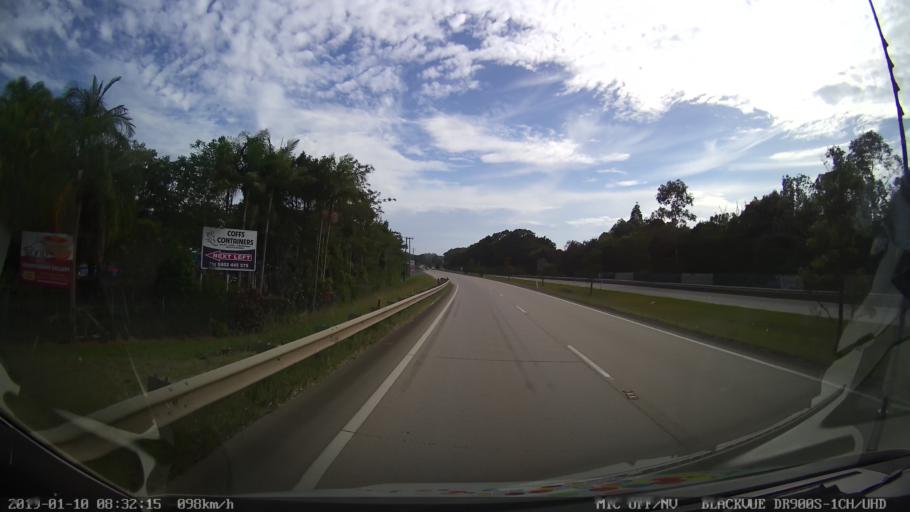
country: AU
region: New South Wales
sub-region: Coffs Harbour
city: Boambee
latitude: -30.3456
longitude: 153.0680
